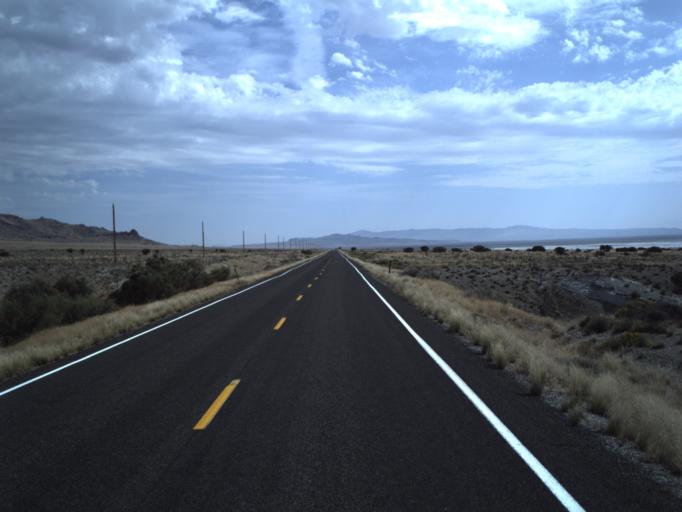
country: US
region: Utah
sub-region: Tooele County
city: Wendover
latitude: 41.4375
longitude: -113.7367
